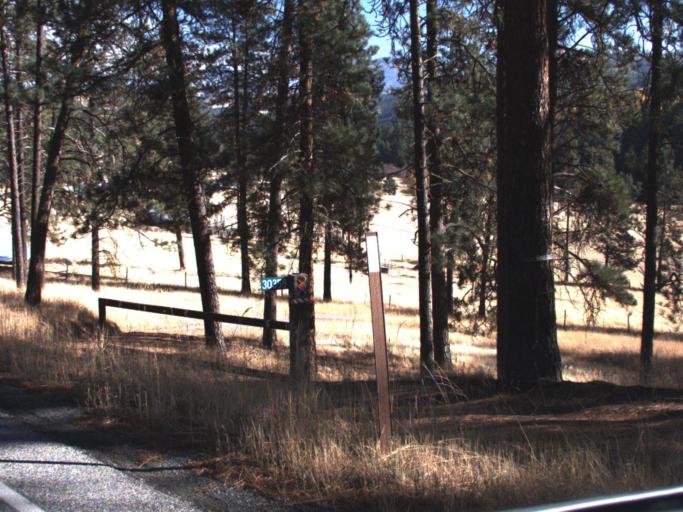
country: US
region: Washington
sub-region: Ferry County
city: Republic
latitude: 48.6488
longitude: -118.7184
